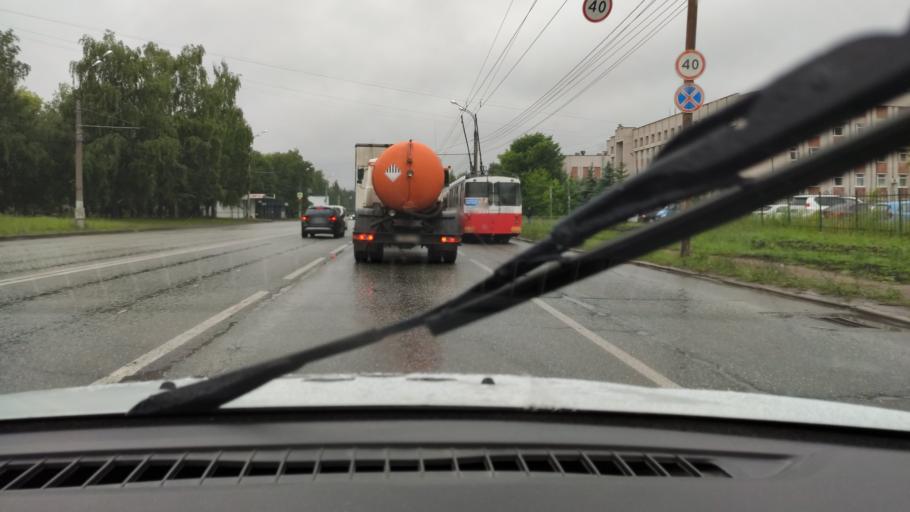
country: RU
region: Udmurtiya
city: Izhevsk
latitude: 56.8866
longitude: 53.2338
